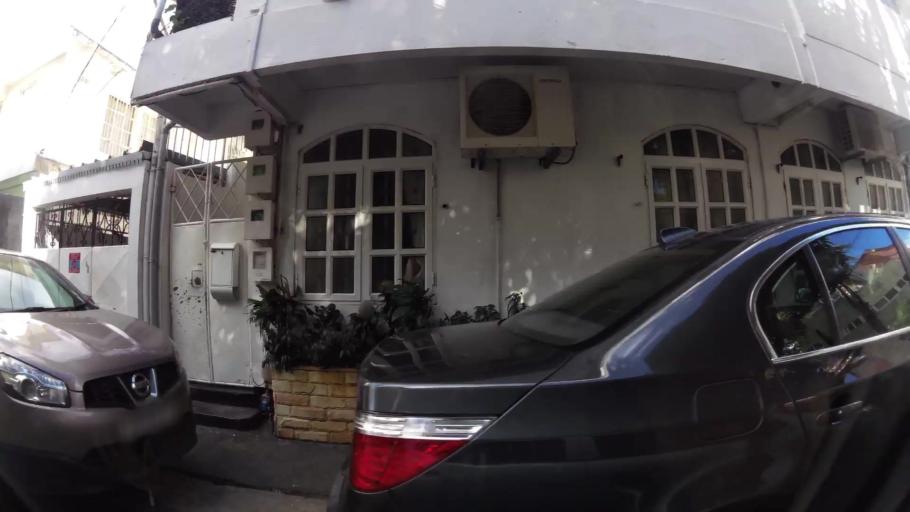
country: MU
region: Port Louis
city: Port Louis
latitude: -20.1546
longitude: 57.5169
